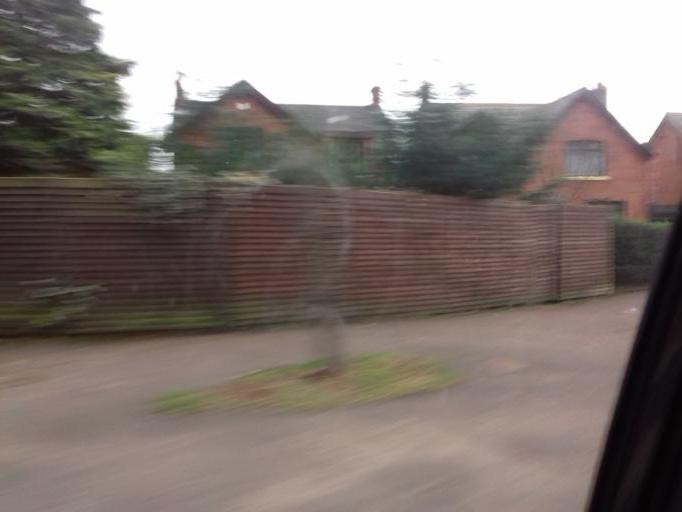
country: GB
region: Northern Ireland
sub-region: City of Belfast
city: Belfast
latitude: 54.6233
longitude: -5.9499
